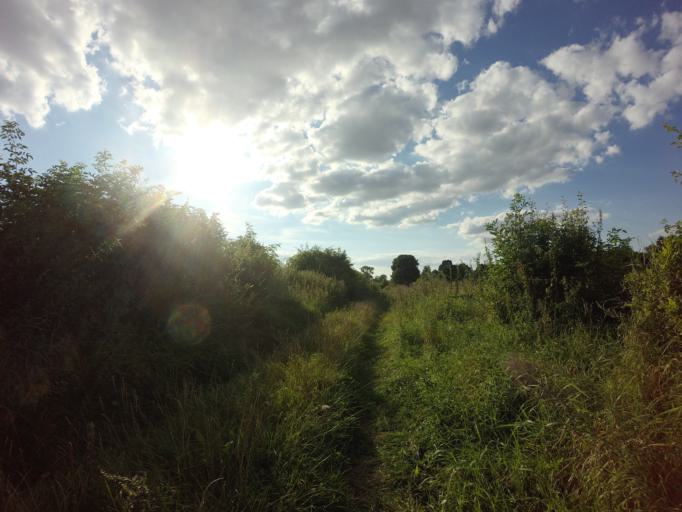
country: PL
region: West Pomeranian Voivodeship
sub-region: Powiat choszczenski
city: Choszczno
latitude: 53.2137
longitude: 15.3961
